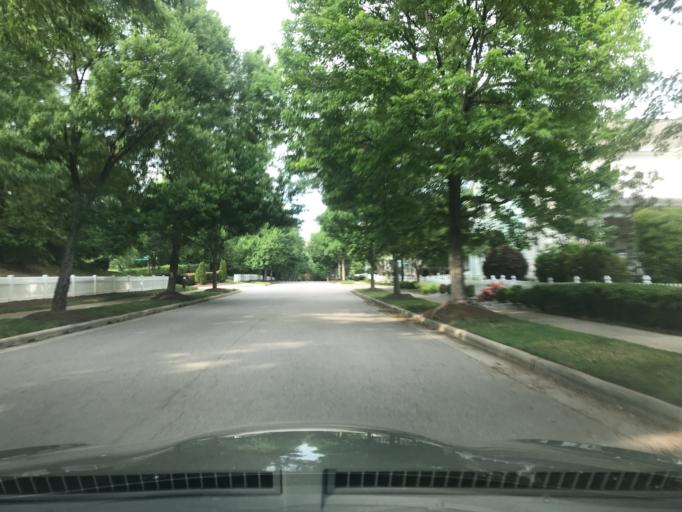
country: US
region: North Carolina
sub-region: Wake County
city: Wake Forest
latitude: 35.9272
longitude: -78.5748
